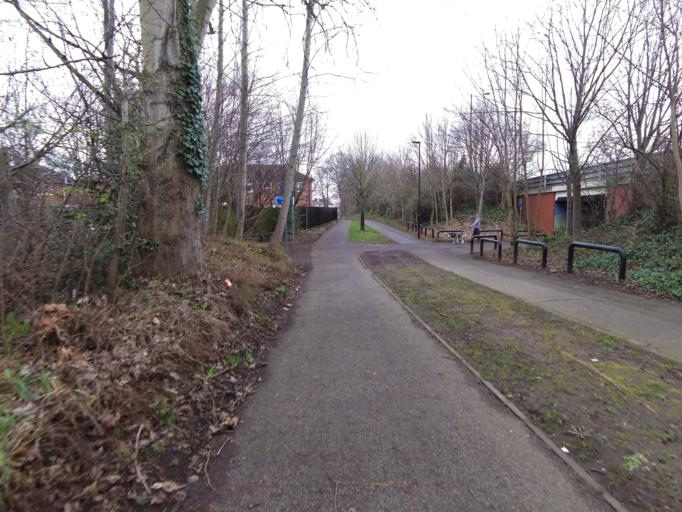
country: GB
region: England
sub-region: Doncaster
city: Bentley
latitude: 53.5340
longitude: -1.1580
